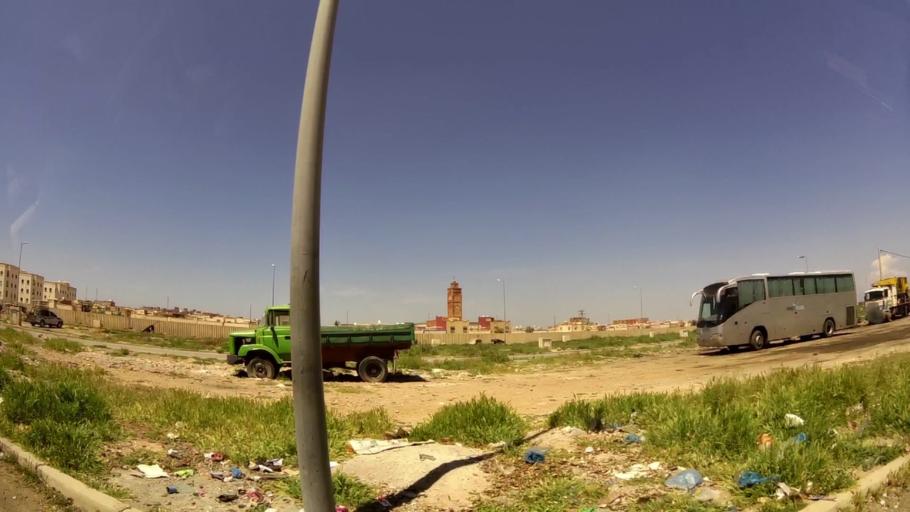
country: MA
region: Oriental
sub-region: Oujda-Angad
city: Oujda
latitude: 34.6934
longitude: -1.9391
